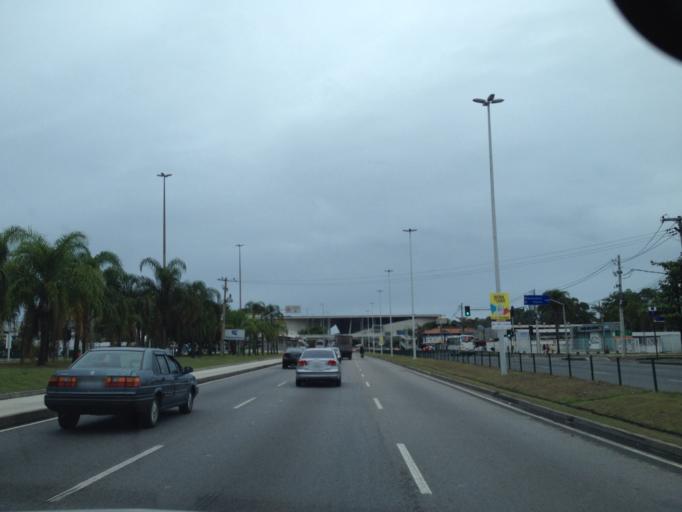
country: BR
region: Rio de Janeiro
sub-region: Rio De Janeiro
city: Rio de Janeiro
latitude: -22.9927
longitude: -43.3661
